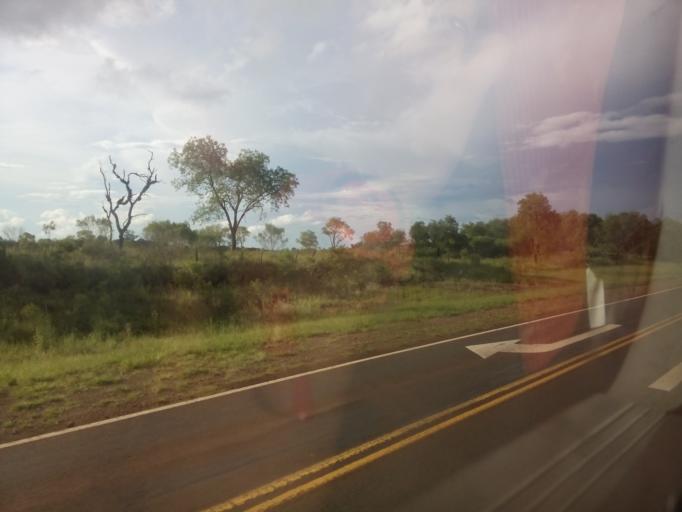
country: AR
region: Misiones
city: Santa Ana
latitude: -27.4169
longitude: -55.6125
